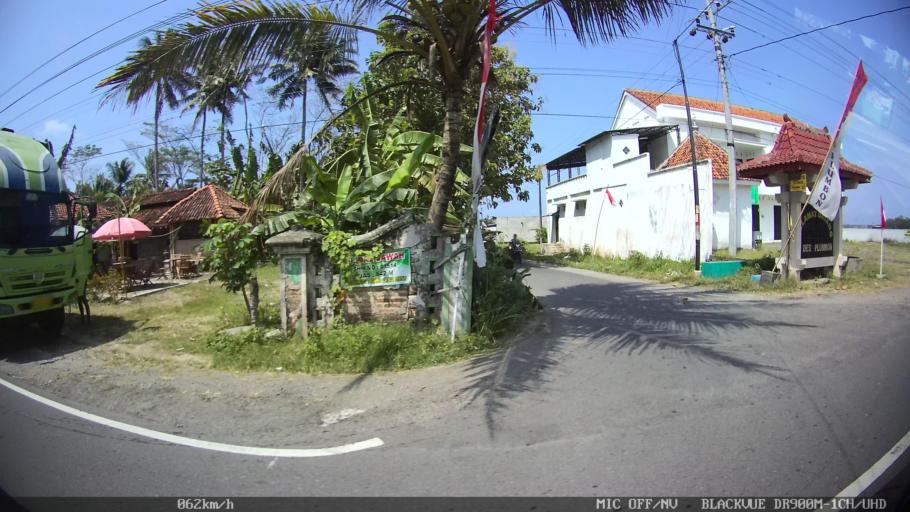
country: ID
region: Daerah Istimewa Yogyakarta
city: Srandakan
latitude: -7.8899
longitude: 110.1031
